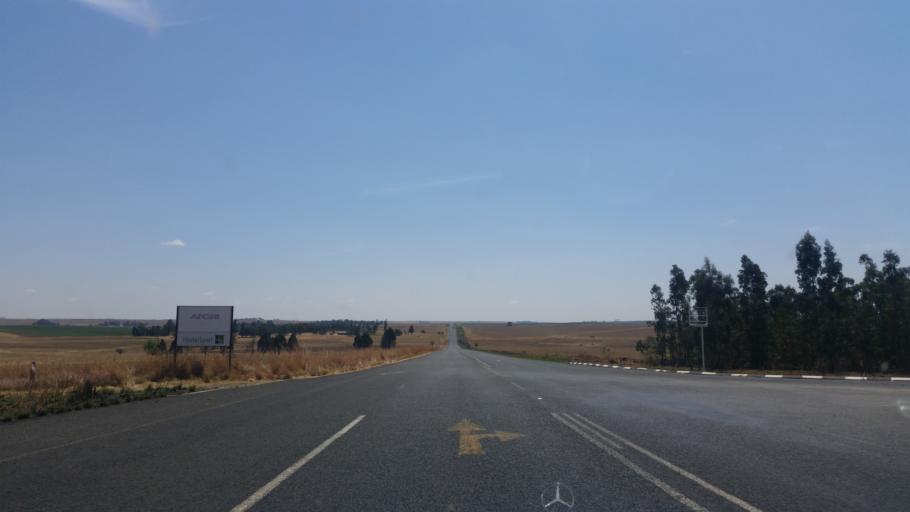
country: ZA
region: Orange Free State
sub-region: Thabo Mofutsanyana District Municipality
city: Phuthaditjhaba
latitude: -28.2000
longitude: 28.6876
